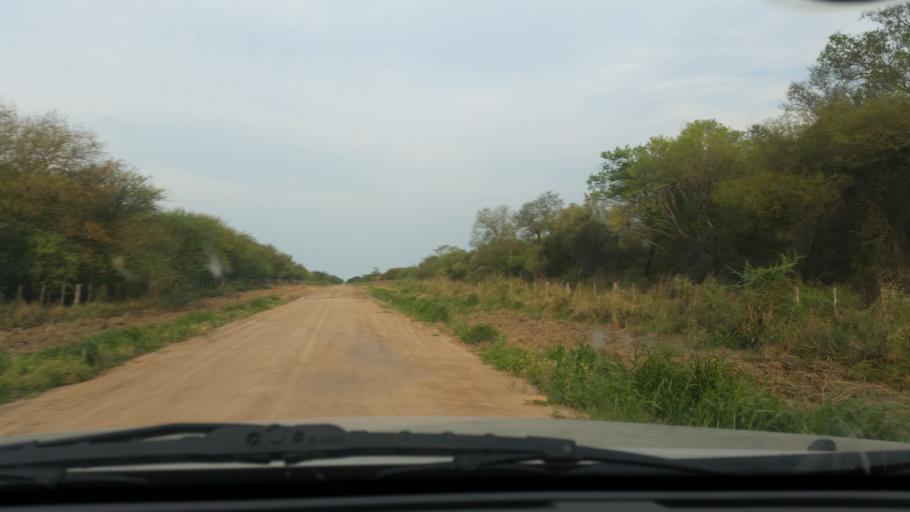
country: PY
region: Boqueron
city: Colonia Menno
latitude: -22.4729
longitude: -59.3173
